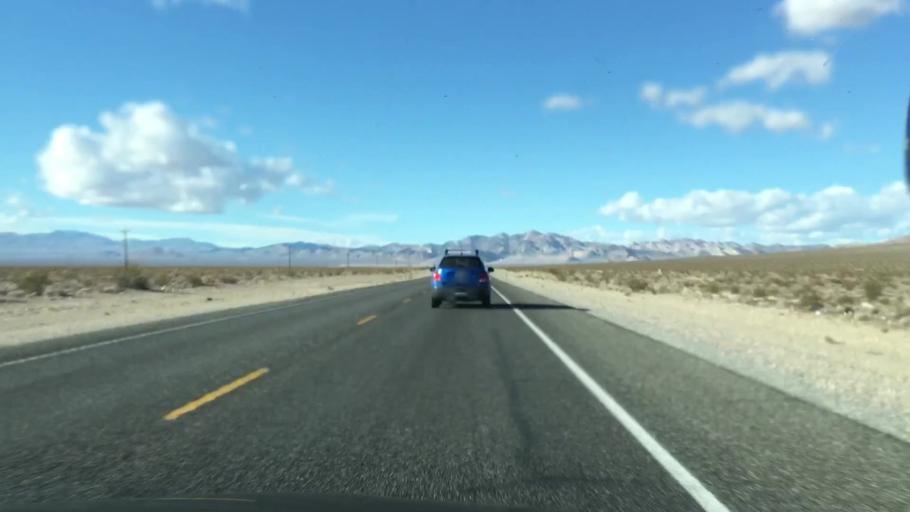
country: US
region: Nevada
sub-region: Nye County
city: Beatty
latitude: 36.8028
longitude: -116.7188
